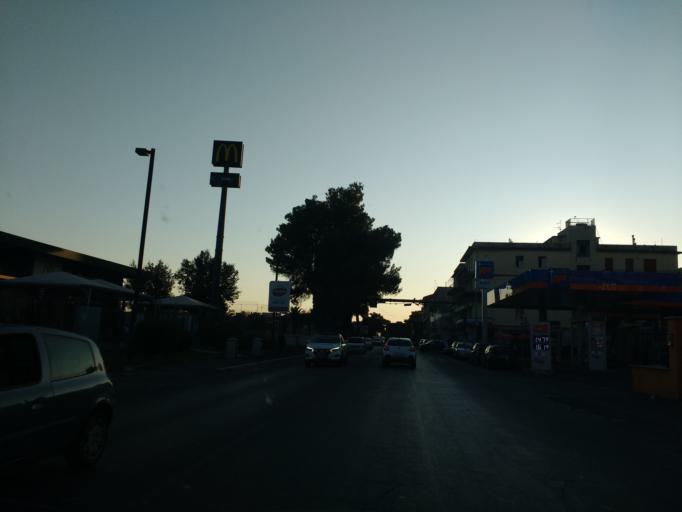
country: IT
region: Latium
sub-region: Citta metropolitana di Roma Capitale
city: Villalba
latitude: 41.9523
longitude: 12.7277
